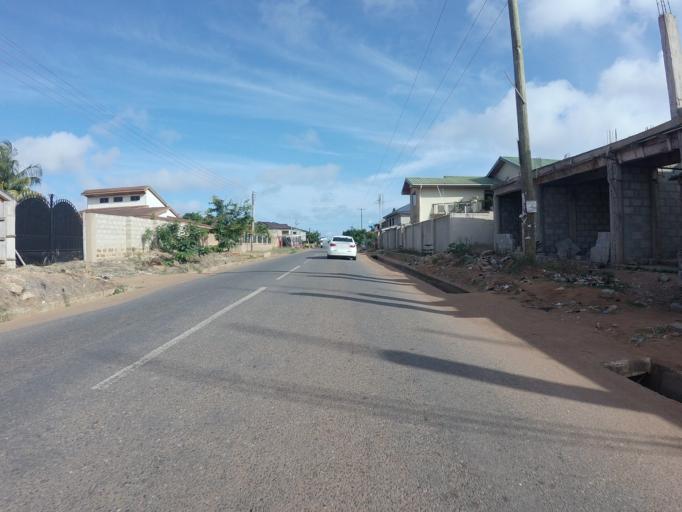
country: GH
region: Greater Accra
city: Teshi Old Town
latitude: 5.5813
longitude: -0.1422
